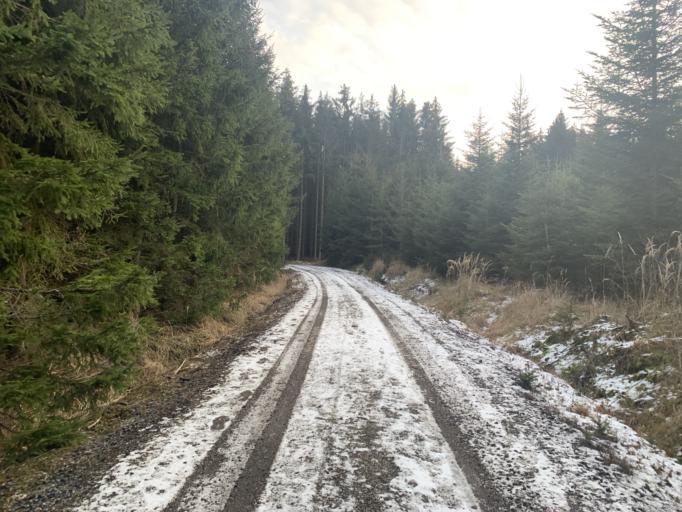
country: CZ
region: Plzensky
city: Zbiroh
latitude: 49.8217
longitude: 13.7980
